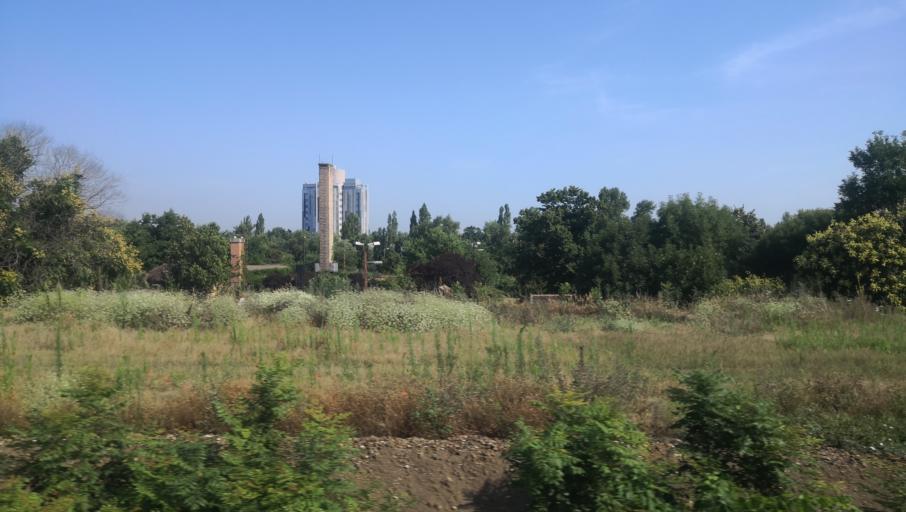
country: HU
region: Budapest
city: Budapest XIV. keruelet
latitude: 47.4896
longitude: 19.1244
